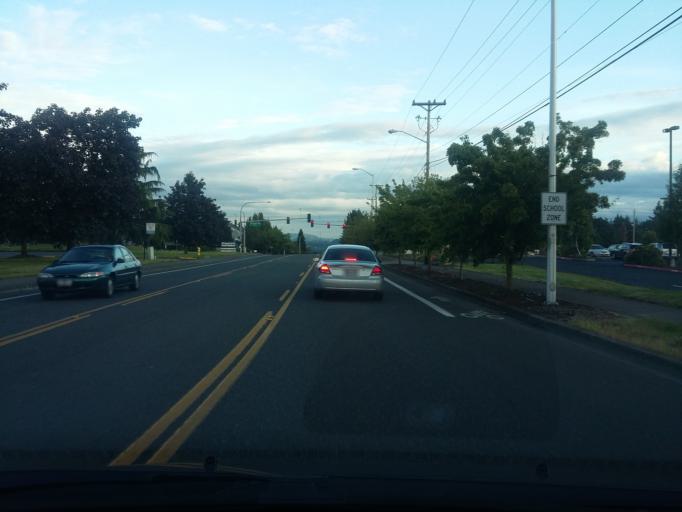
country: US
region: Washington
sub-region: Clark County
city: Orchards
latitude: 45.6156
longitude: -122.5613
